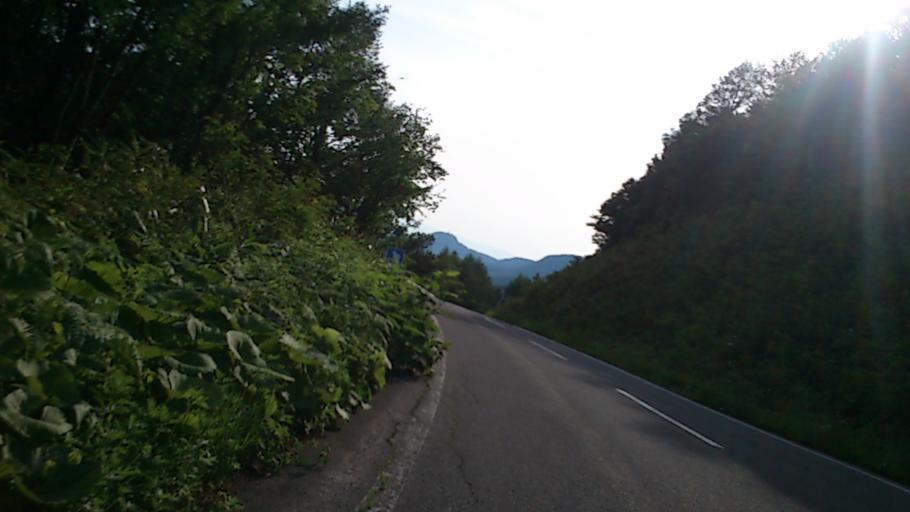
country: JP
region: Aomori
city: Aomori Shi
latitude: 40.6490
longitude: 140.7790
